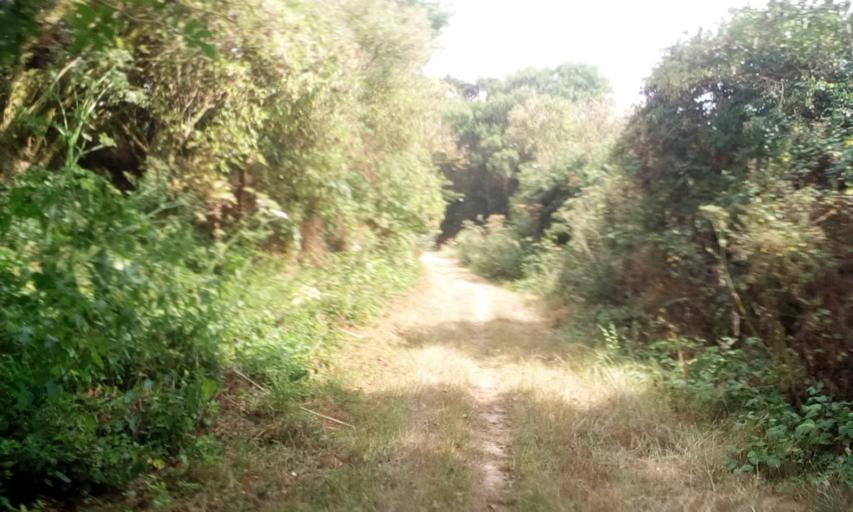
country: FR
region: Lower Normandy
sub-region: Departement du Calvados
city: Douvres-la-Delivrande
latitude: 49.2938
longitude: -0.3974
